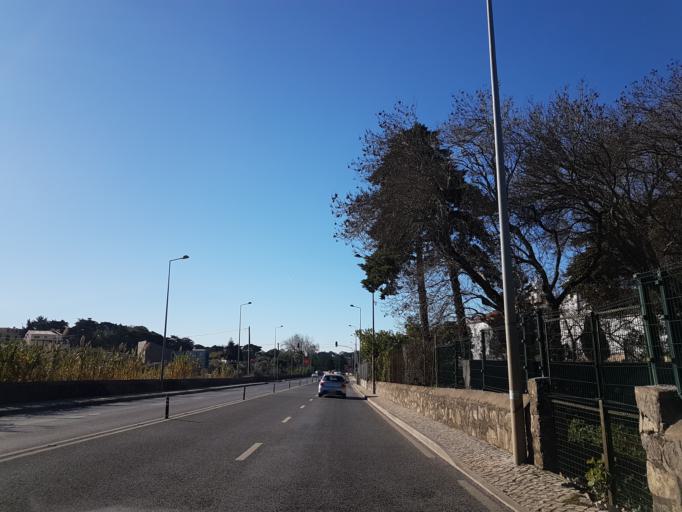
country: PT
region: Lisbon
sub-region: Sintra
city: Sintra
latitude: 38.7697
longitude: -9.3834
